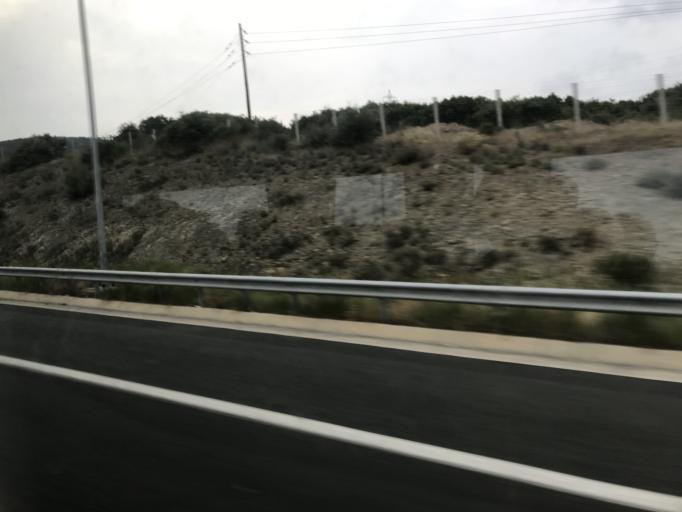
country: GR
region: East Macedonia and Thrace
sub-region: Nomos Evrou
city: Alexandroupoli
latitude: 40.8601
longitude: 25.7453
